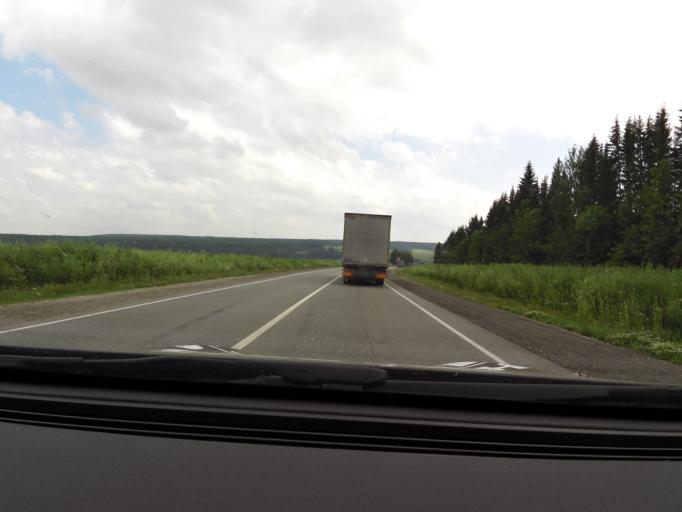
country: RU
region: Perm
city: Suksun
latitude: 57.0714
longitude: 57.4168
